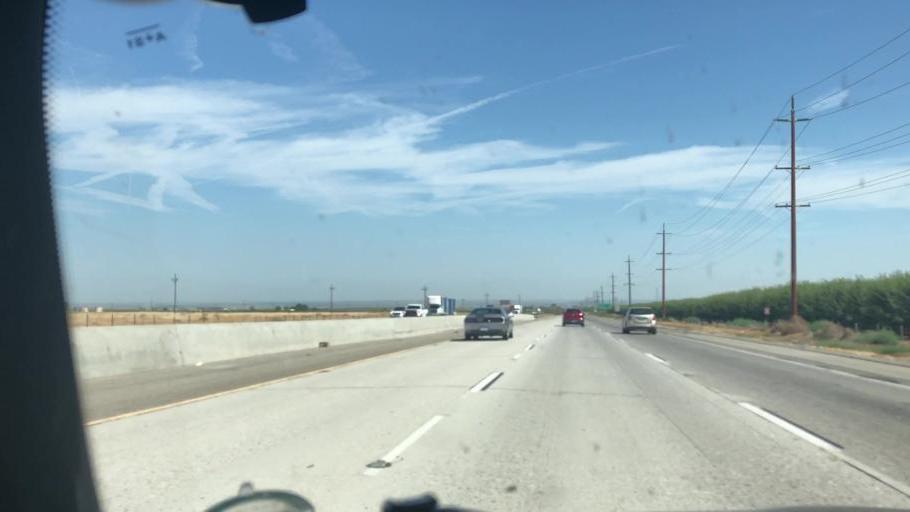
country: US
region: California
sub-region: Kern County
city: Frazier Park
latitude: 35.0210
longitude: -118.9562
